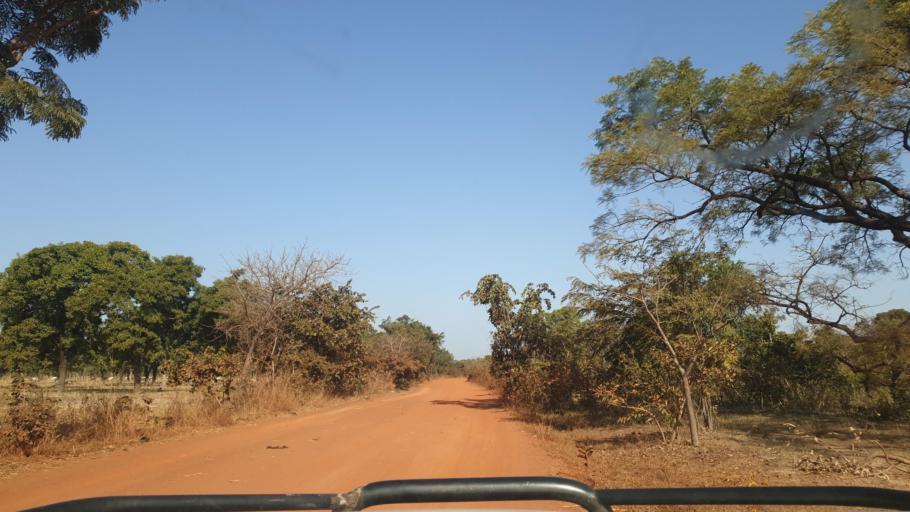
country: ML
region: Sikasso
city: Kolondieba
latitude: 11.7440
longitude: -6.8961
